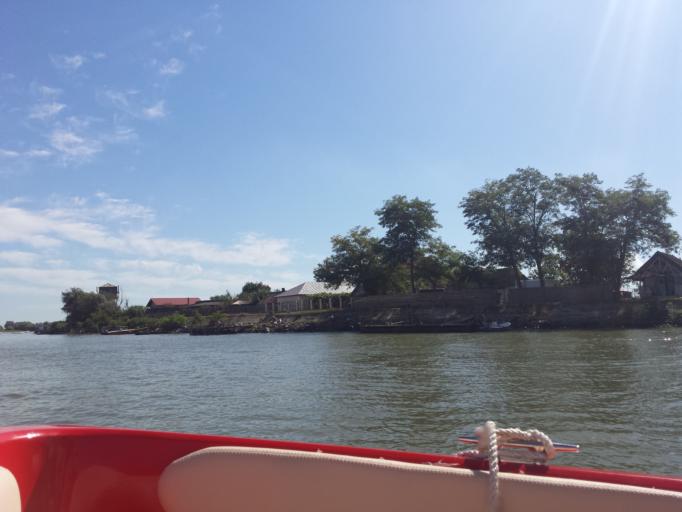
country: RO
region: Tulcea
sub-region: Comuna Crisan
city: Crisan
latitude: 45.2264
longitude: 29.2388
